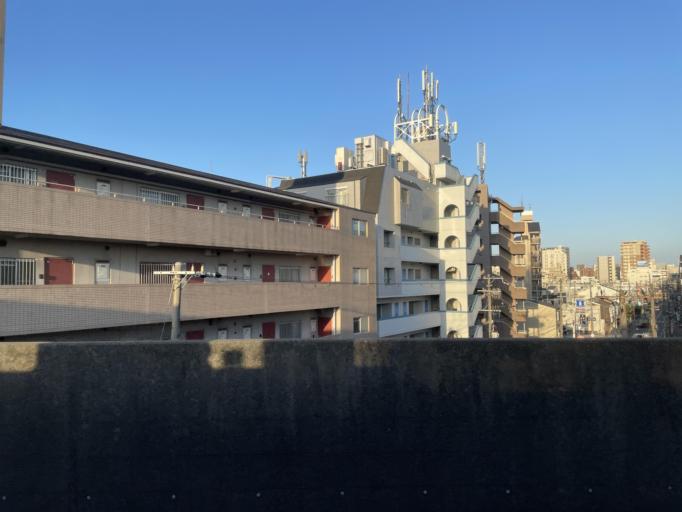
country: JP
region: Osaka
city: Osaka-shi
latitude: 34.6372
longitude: 135.5271
